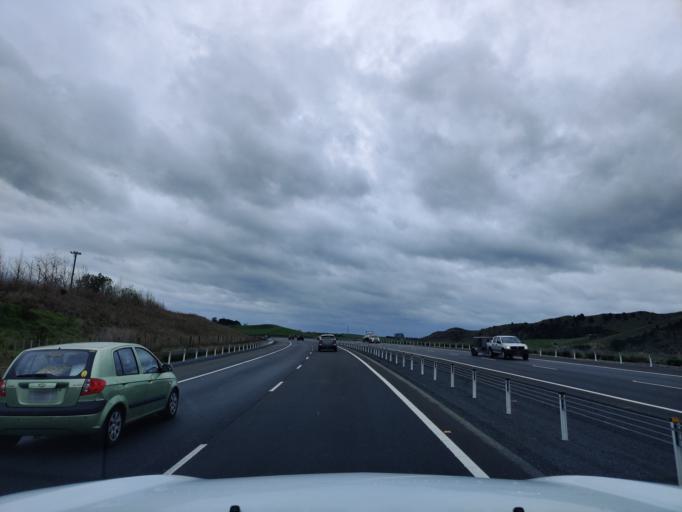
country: NZ
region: Waikato
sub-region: Waikato District
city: Te Kauwhata
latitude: -37.5310
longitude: 175.1901
